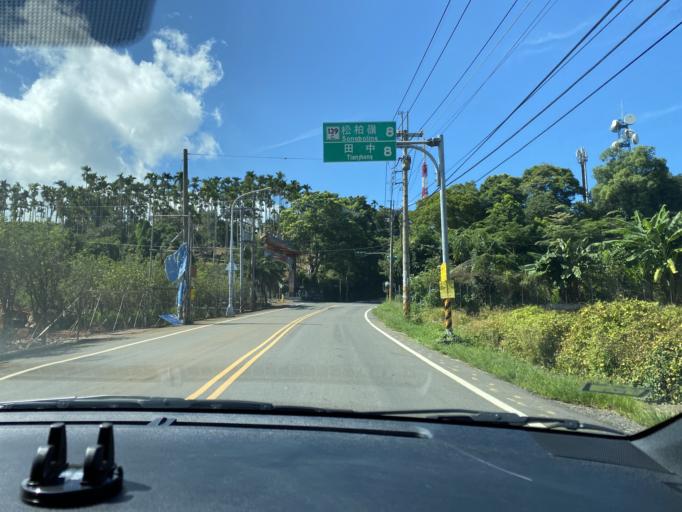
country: TW
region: Taiwan
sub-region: Nantou
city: Nantou
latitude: 23.8970
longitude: 120.6373
